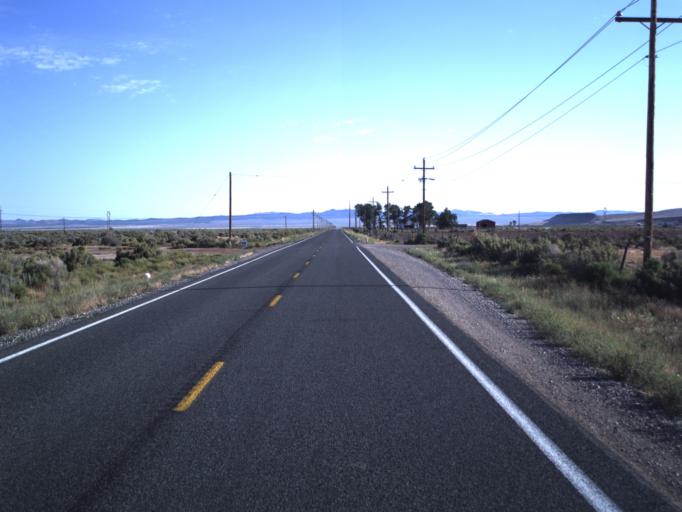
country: US
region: Utah
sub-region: Iron County
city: Enoch
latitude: 37.7940
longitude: -113.0506
